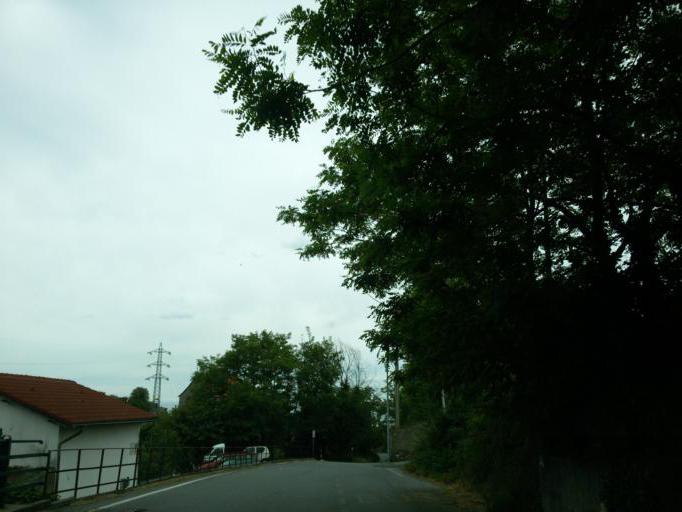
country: IT
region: Liguria
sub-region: Provincia di Genova
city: San Teodoro
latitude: 44.4230
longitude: 8.9038
